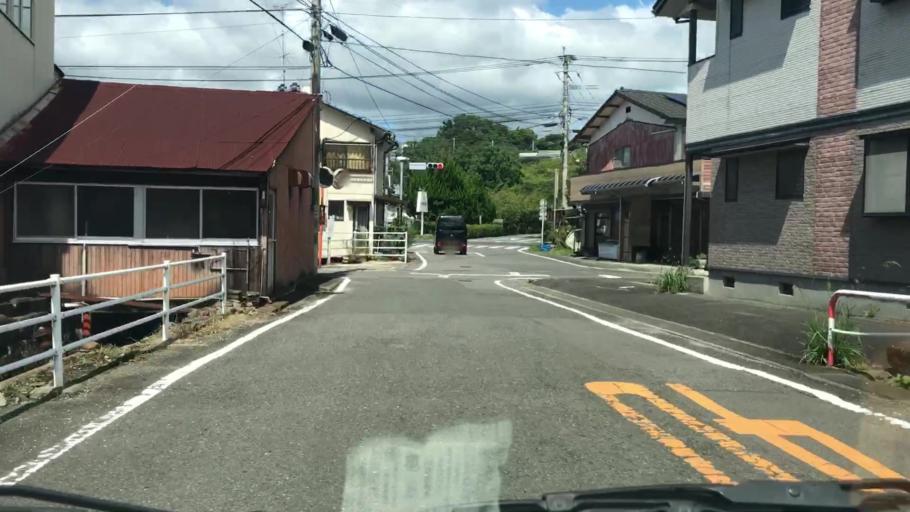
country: JP
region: Saga Prefecture
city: Takeocho-takeo
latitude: 33.2198
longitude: 130.0733
